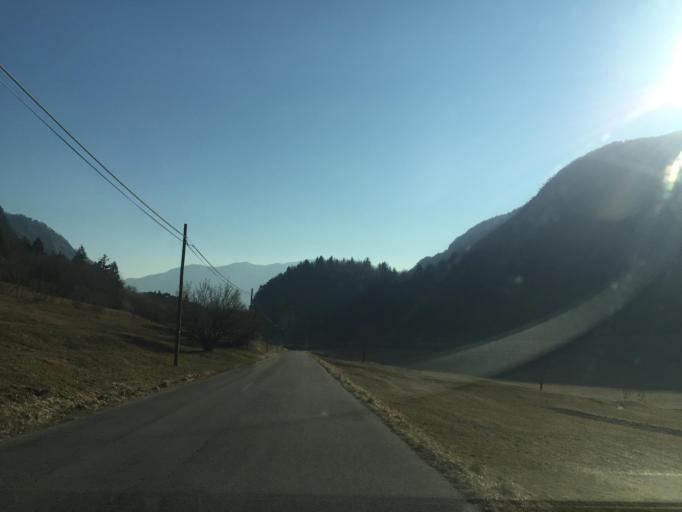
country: IT
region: Friuli Venezia Giulia
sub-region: Provincia di Udine
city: Tolmezzo
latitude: 46.4256
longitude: 13.0526
